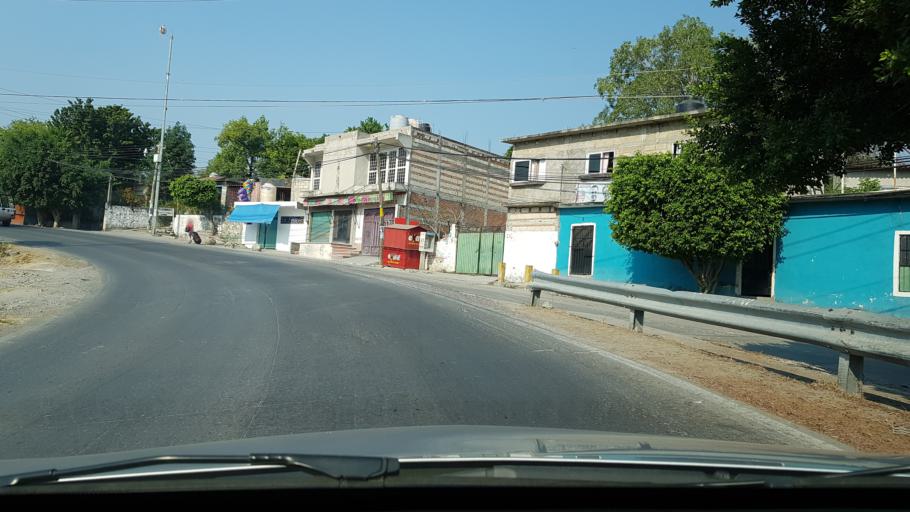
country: MX
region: Morelos
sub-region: Tlaquiltenango
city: Alfredo V. Bonfil (Chacampalco)
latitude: 18.6579
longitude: -99.1542
